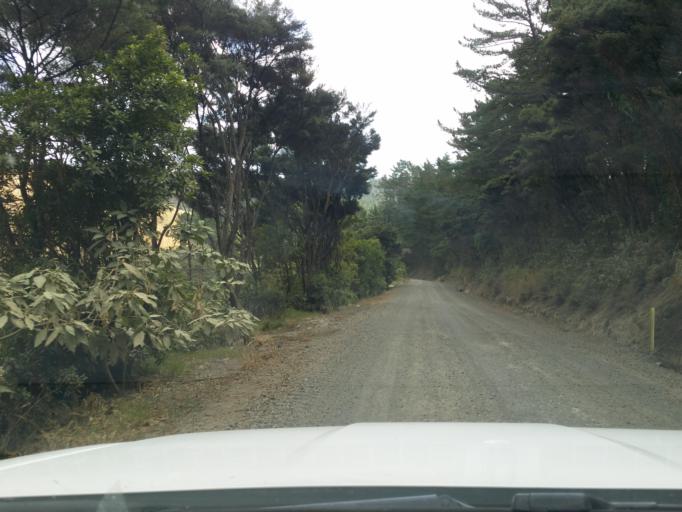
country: NZ
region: Auckland
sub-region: Auckland
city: Wellsford
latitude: -36.3110
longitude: 174.1274
